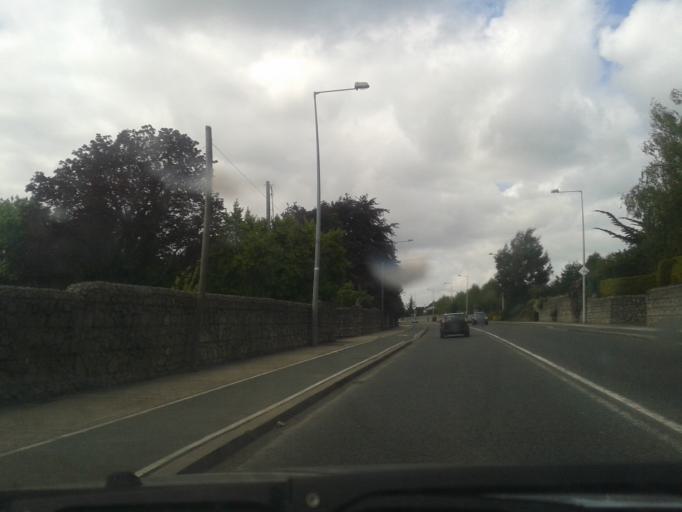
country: IE
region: Leinster
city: Loughlinstown
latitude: 53.2625
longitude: -6.1310
